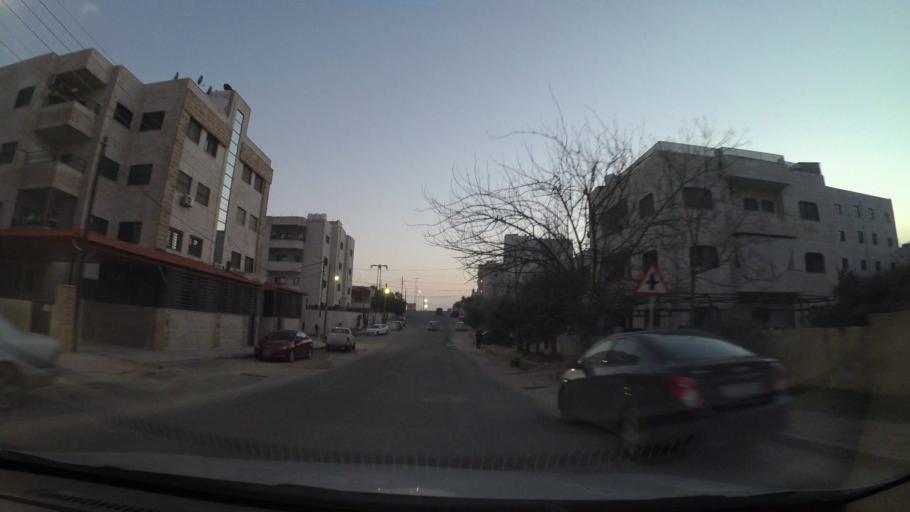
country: JO
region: Amman
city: Al Bunayyat ash Shamaliyah
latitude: 31.8880
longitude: 35.9241
